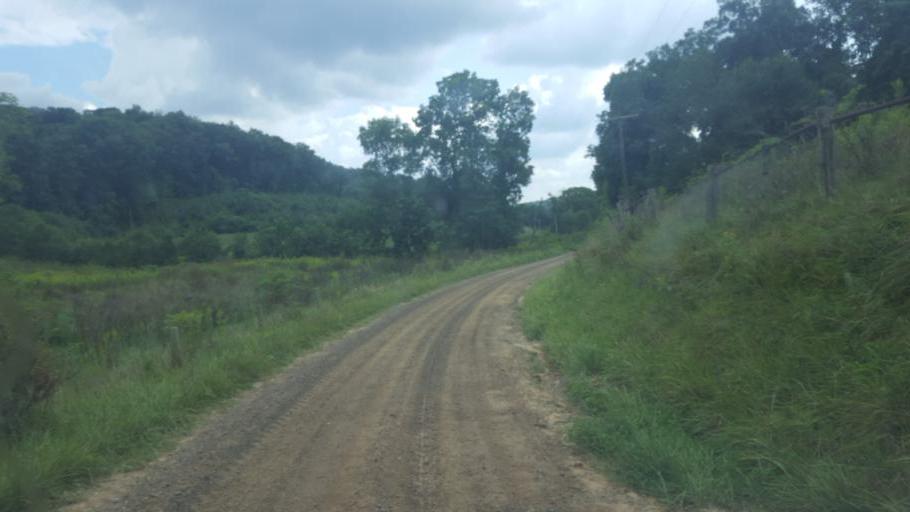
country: US
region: Ohio
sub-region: Knox County
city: Oak Hill
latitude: 40.3965
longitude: -82.2408
